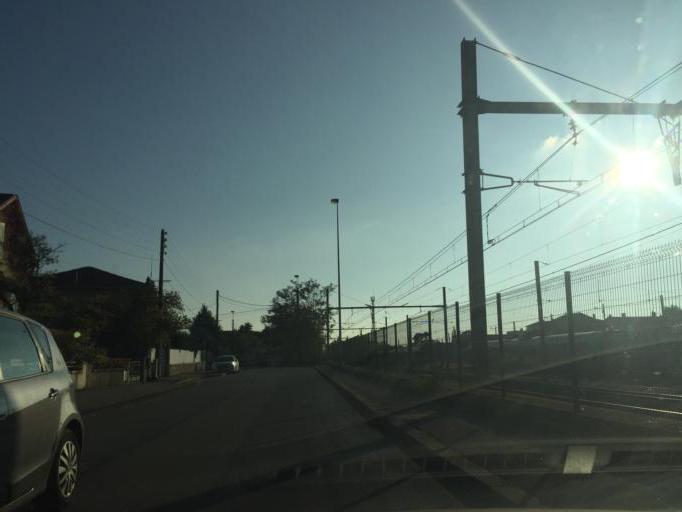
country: FR
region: Rhone-Alpes
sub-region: Departement de la Drome
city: Valence
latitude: 44.9188
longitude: 4.8909
